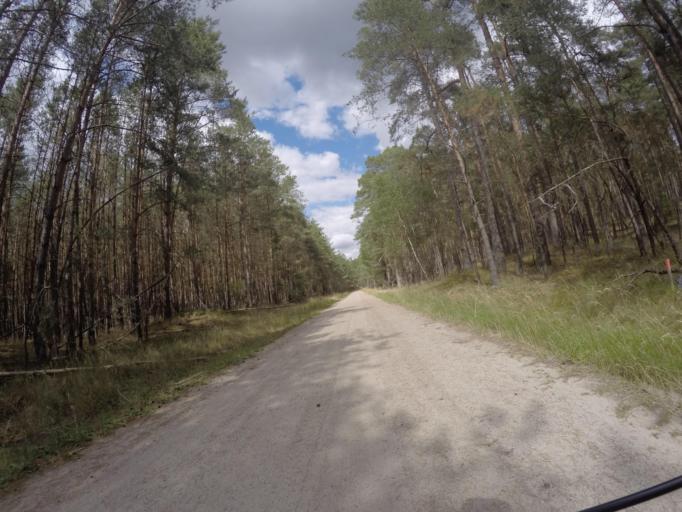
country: DE
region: Lower Saxony
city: Neu Darchau
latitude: 53.2586
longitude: 10.9751
